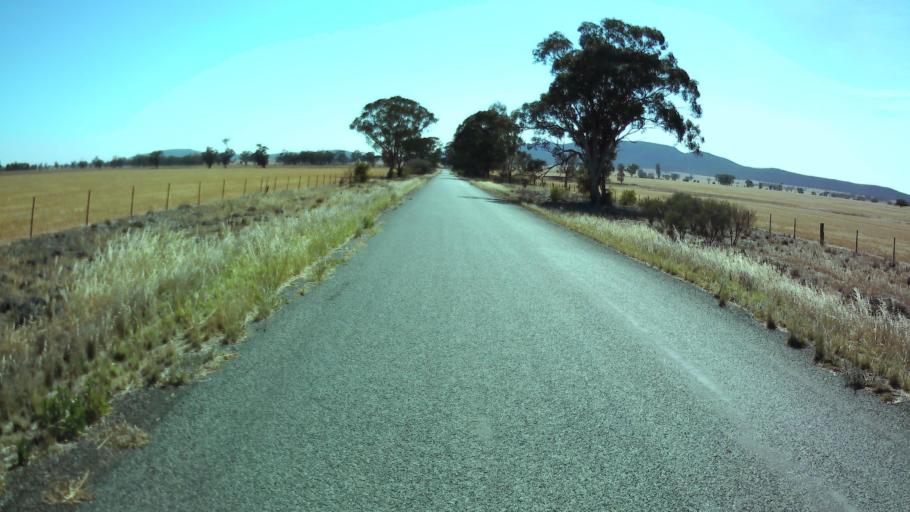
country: AU
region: New South Wales
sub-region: Weddin
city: Grenfell
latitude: -33.7509
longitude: 147.8695
